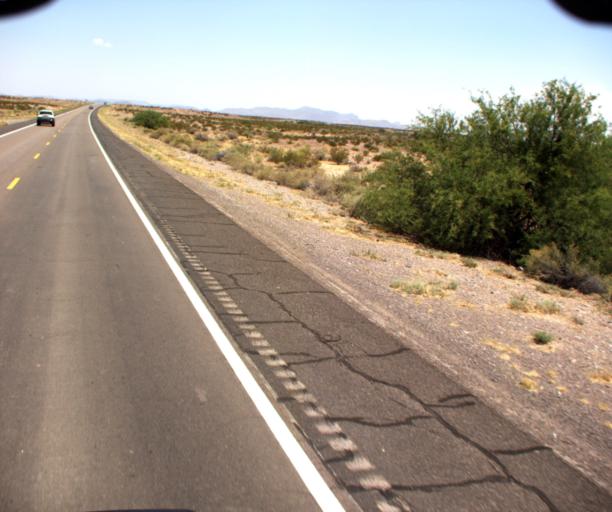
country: US
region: Arizona
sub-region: Graham County
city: Safford
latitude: 32.7977
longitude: -109.5614
